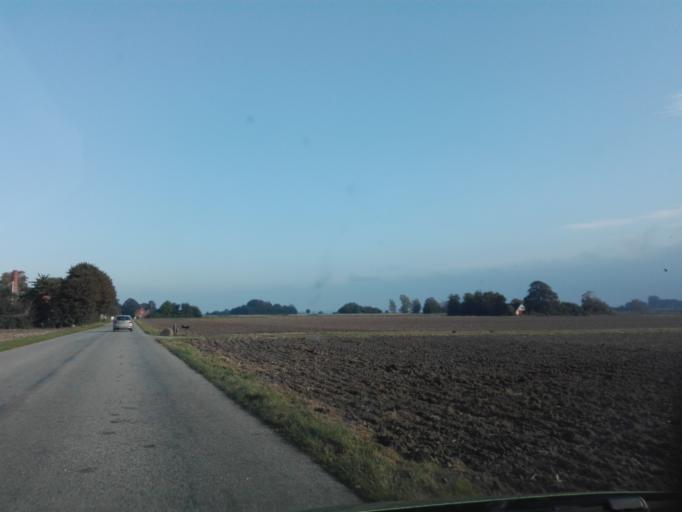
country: DK
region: Central Jutland
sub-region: Odder Kommune
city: Odder
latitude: 55.8910
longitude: 10.1795
